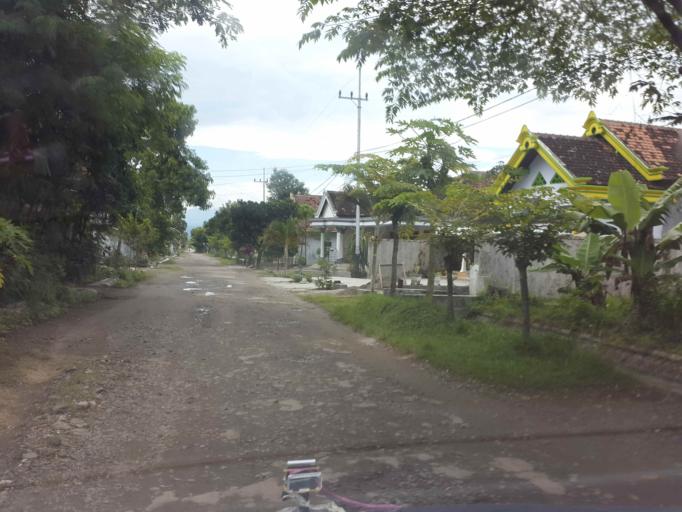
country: ID
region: East Java
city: Ponorogo
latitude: -7.7856
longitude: 111.4959
